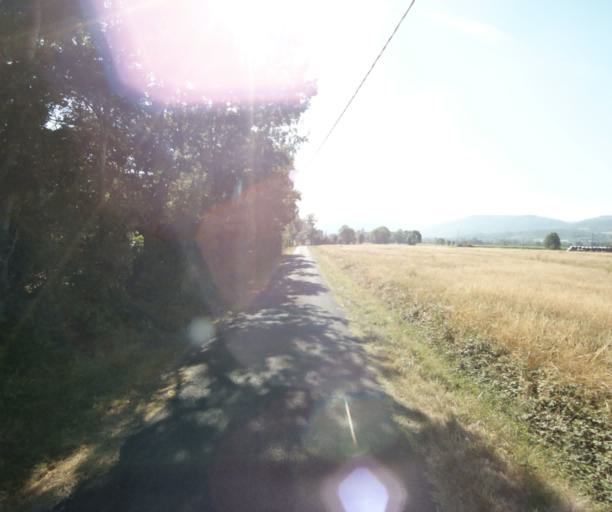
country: FR
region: Midi-Pyrenees
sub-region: Departement de la Haute-Garonne
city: Revel
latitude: 43.4619
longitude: 2.0246
